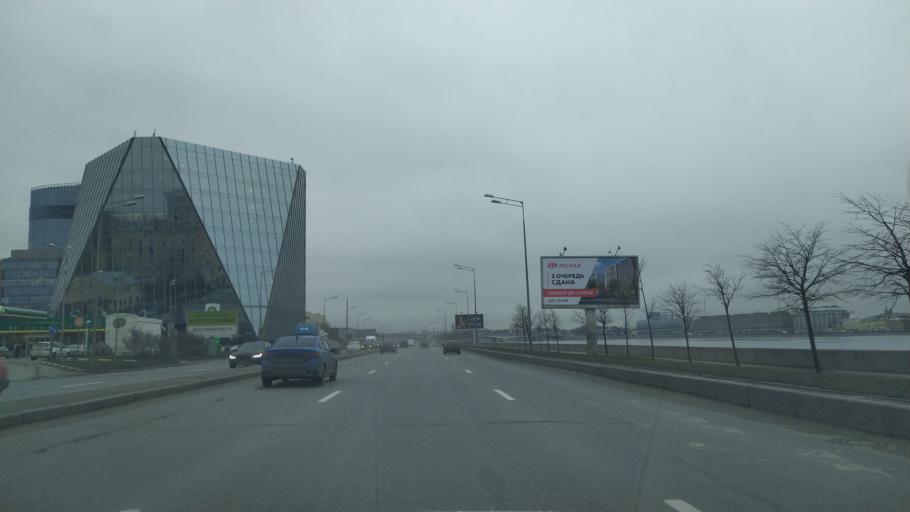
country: RU
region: St.-Petersburg
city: Centralniy
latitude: 59.9355
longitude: 30.4019
